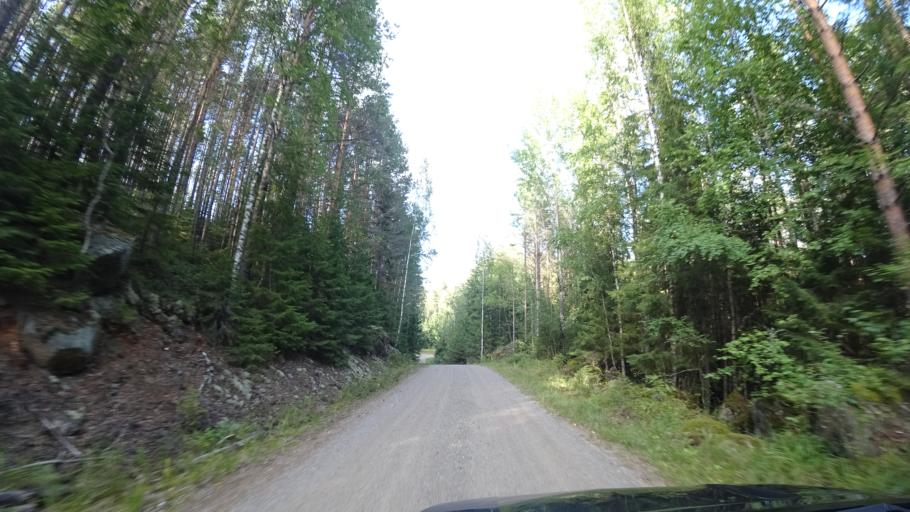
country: FI
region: Paijanne Tavastia
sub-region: Lahti
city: Auttoinen
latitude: 61.2244
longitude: 25.1923
